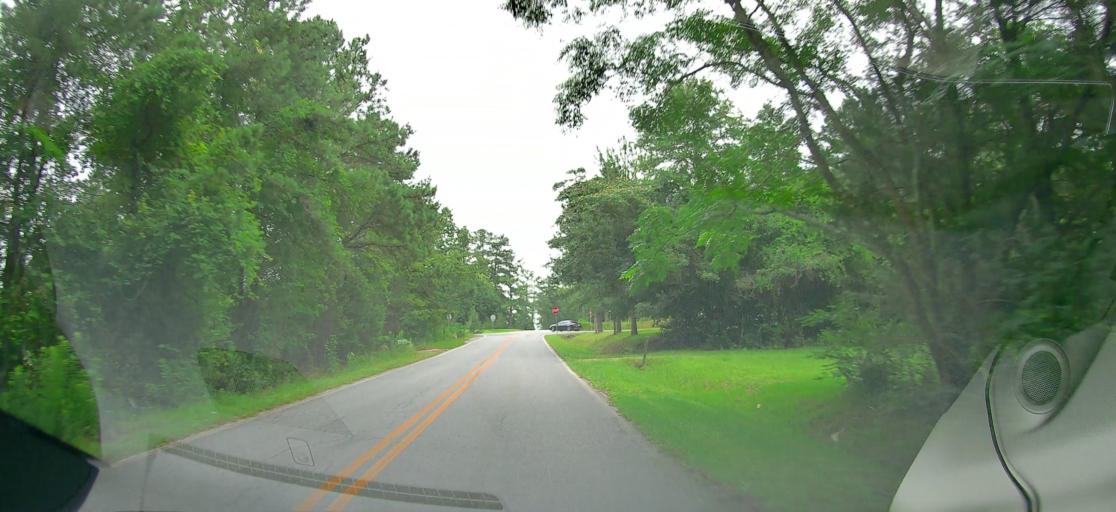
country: US
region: Georgia
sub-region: Bibb County
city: West Point
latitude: 32.7713
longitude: -83.7790
